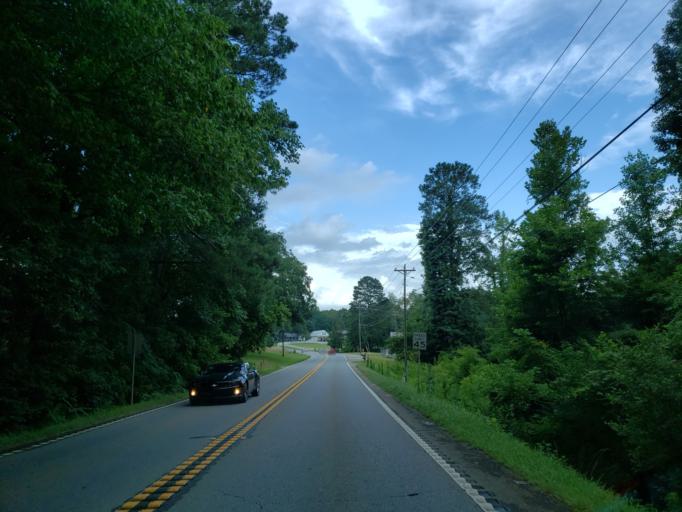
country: US
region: Georgia
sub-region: Cherokee County
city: Holly Springs
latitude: 34.1793
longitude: -84.4312
